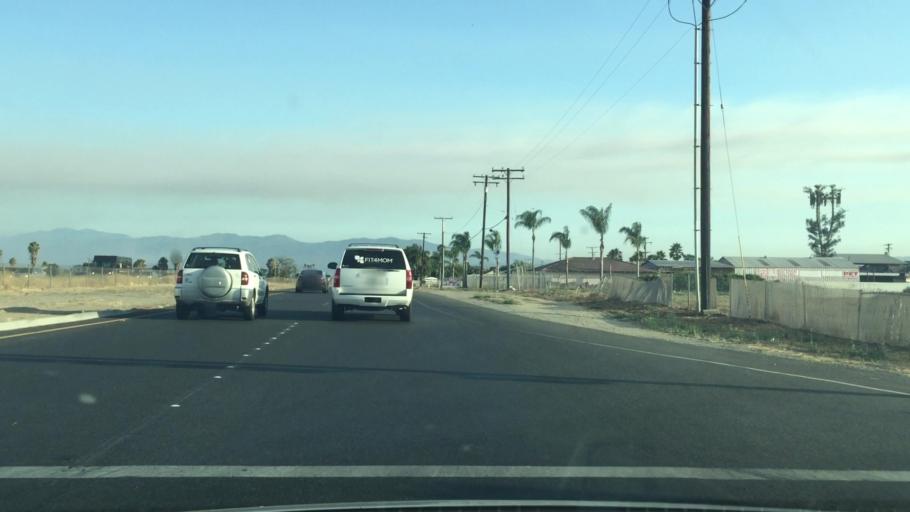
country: US
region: California
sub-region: San Bernardino County
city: Chino
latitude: 34.0191
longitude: -117.6509
